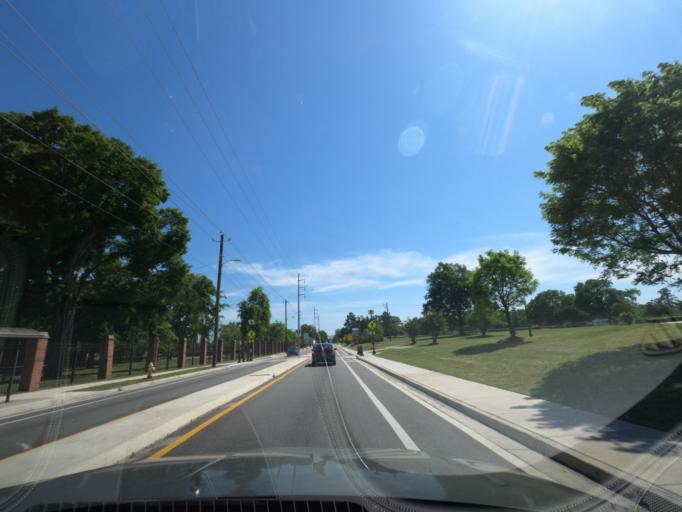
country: US
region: Georgia
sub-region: Richmond County
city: Augusta
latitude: 33.4706
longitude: -81.9965
